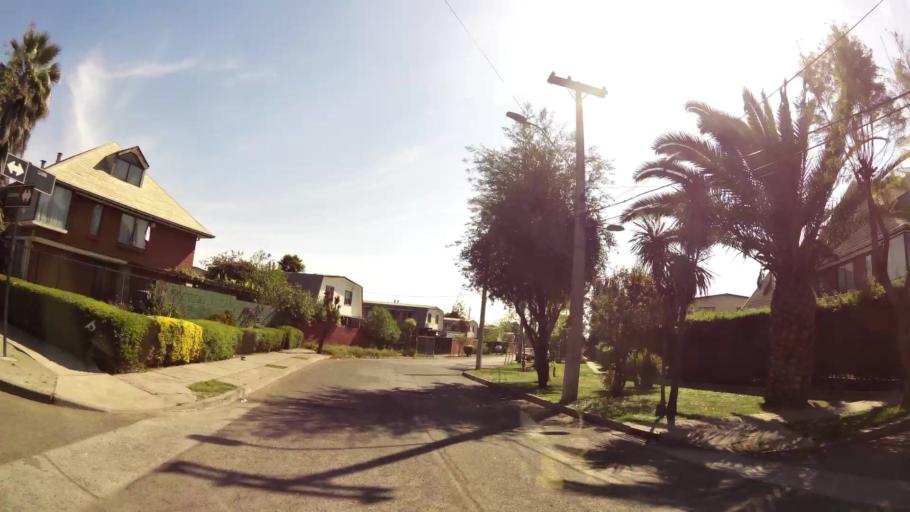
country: CL
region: Santiago Metropolitan
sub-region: Provincia de Santiago
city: Villa Presidente Frei, Nunoa, Santiago, Chile
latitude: -33.4956
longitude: -70.5763
